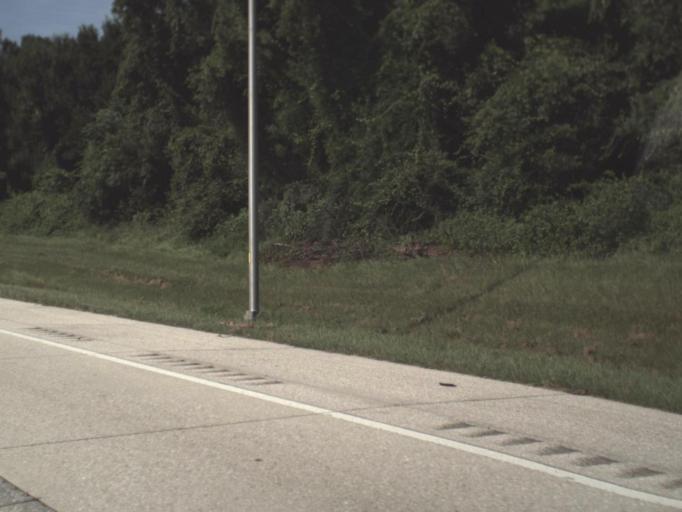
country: US
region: Florida
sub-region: Hillsborough County
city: Mango
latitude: 27.9895
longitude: -82.3266
